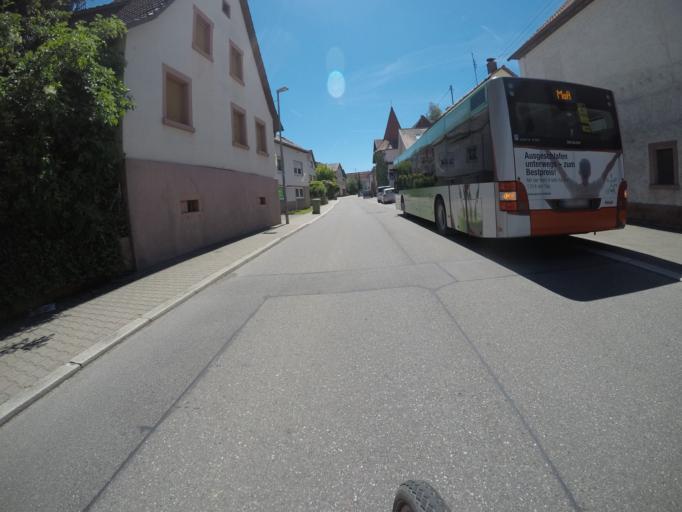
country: DE
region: Baden-Wuerttemberg
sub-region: Karlsruhe Region
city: Friolzheim
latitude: 48.8061
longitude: 8.8220
